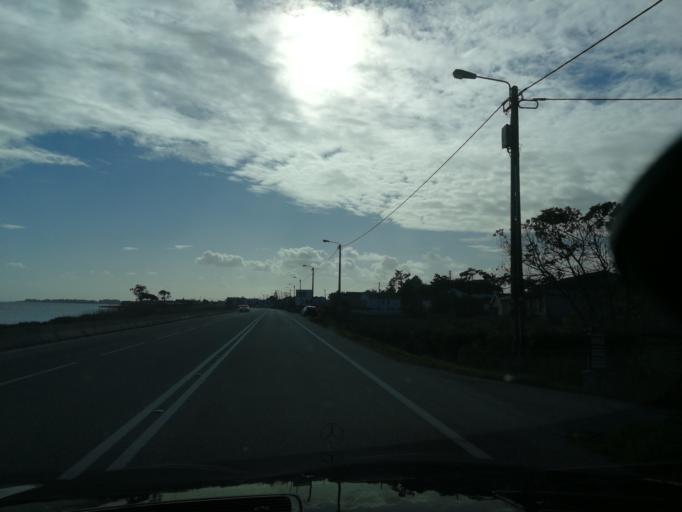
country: PT
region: Aveiro
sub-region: Murtosa
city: Murtosa
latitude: 40.7787
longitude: -8.6907
